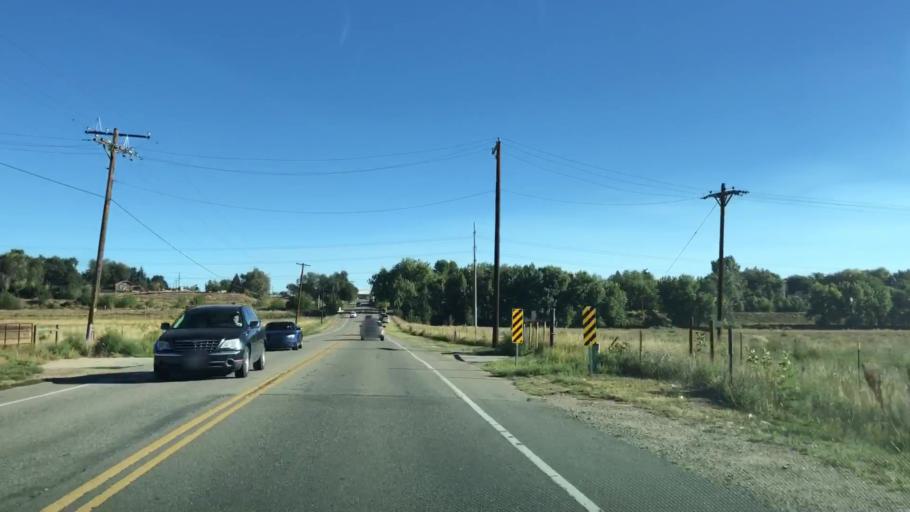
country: US
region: Colorado
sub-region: Larimer County
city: Loveland
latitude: 40.4030
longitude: -105.1223
